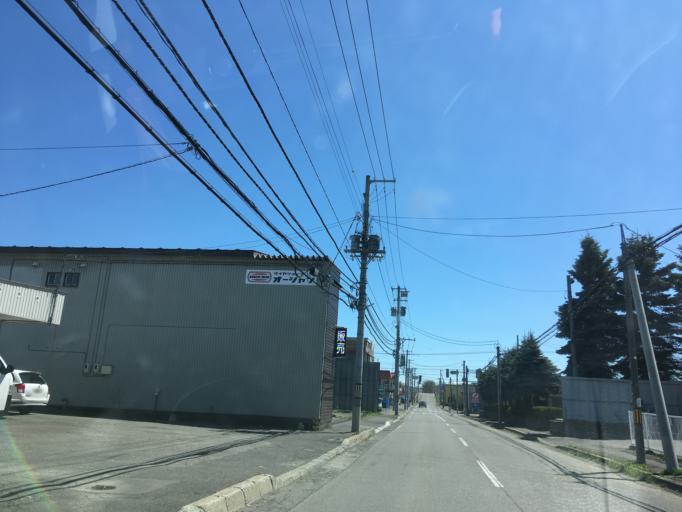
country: JP
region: Hokkaido
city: Obihiro
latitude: 42.9285
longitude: 143.1772
